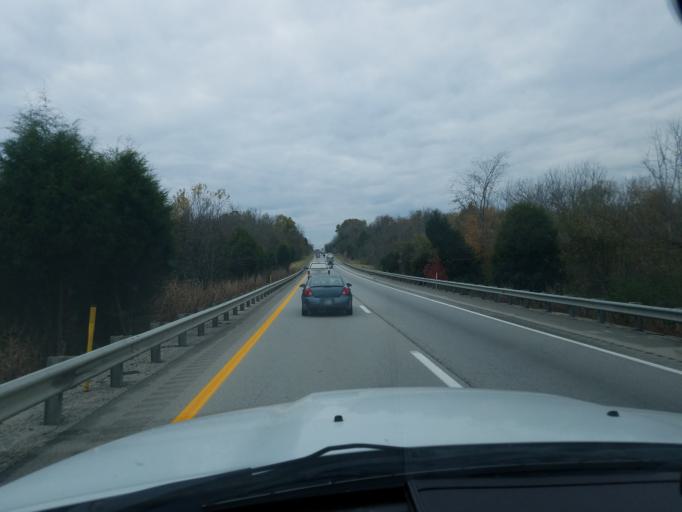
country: US
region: Kentucky
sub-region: Oldham County
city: La Grange
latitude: 38.4322
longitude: -85.3176
